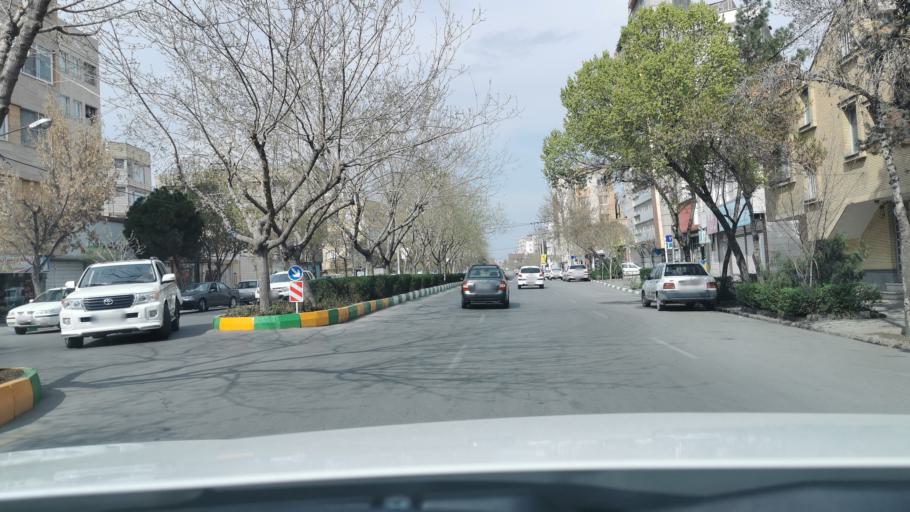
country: IR
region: Razavi Khorasan
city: Mashhad
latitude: 36.3061
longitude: 59.5868
